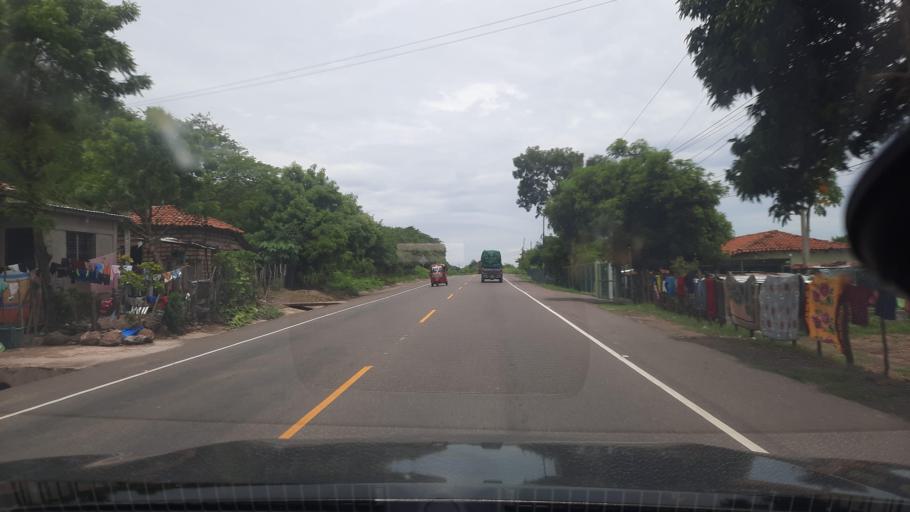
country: HN
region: Valle
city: Goascoran
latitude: 13.5536
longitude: -87.6480
